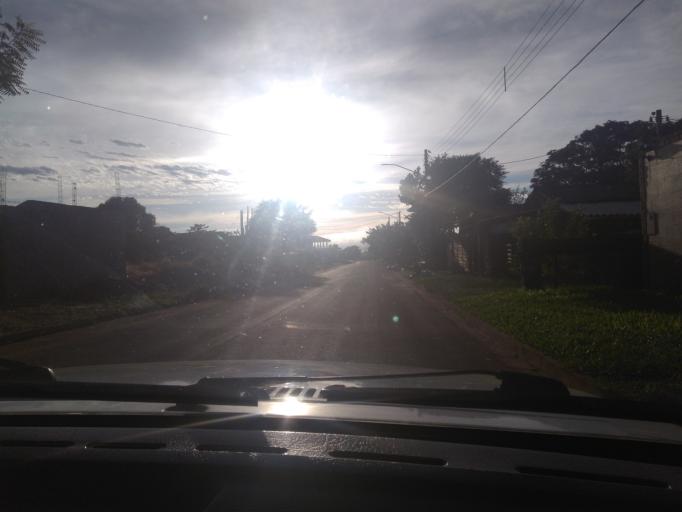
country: BR
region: Mato Grosso do Sul
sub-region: Ponta Pora
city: Ponta Pora
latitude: -22.5118
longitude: -55.7291
